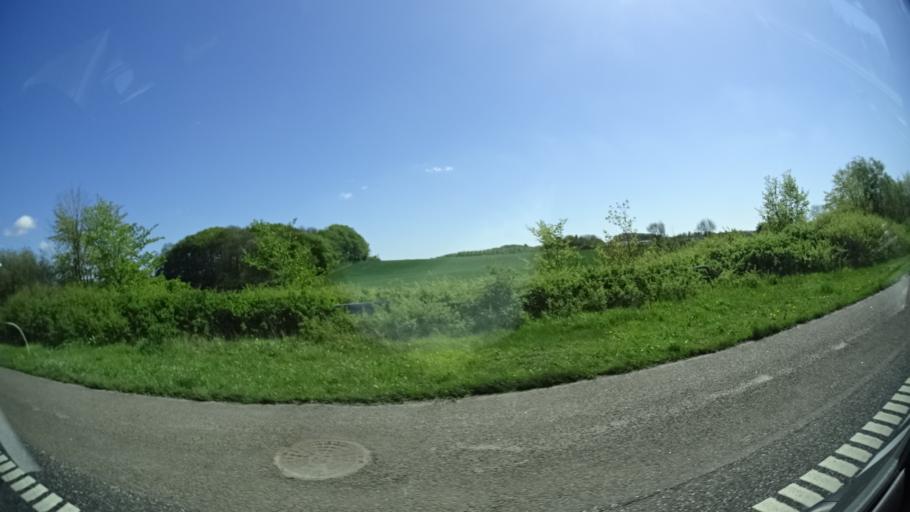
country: DK
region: Central Jutland
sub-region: Arhus Kommune
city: Kolt
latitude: 56.1217
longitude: 10.0895
